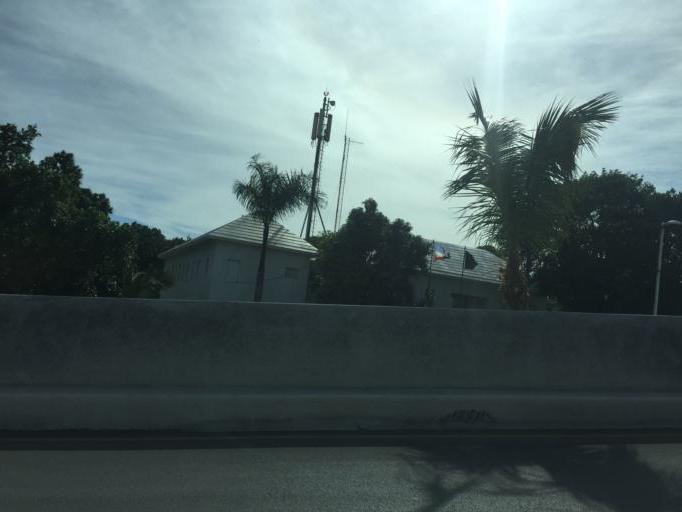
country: DO
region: San Juan
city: Punta Cana
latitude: 18.5620
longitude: -68.3664
